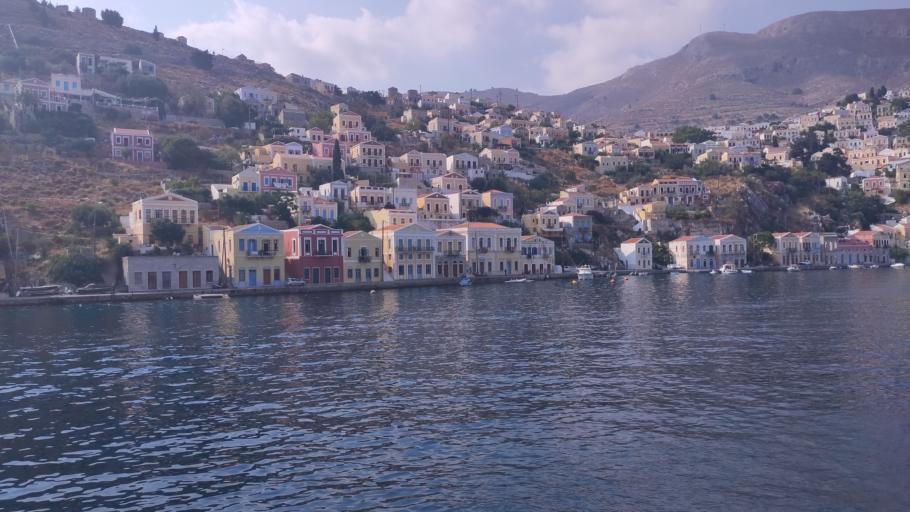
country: GR
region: South Aegean
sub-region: Nomos Dodekanisou
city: Symi
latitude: 36.6183
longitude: 27.8412
